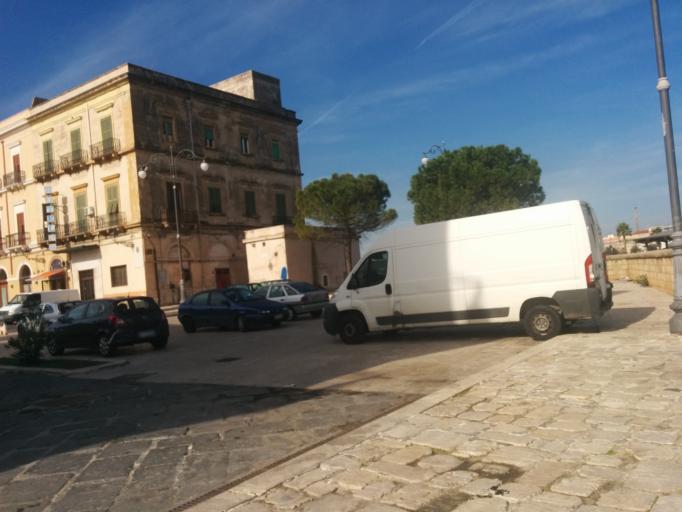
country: IT
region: Apulia
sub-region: Provincia di Taranto
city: Statte
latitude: 40.4795
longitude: 17.2280
